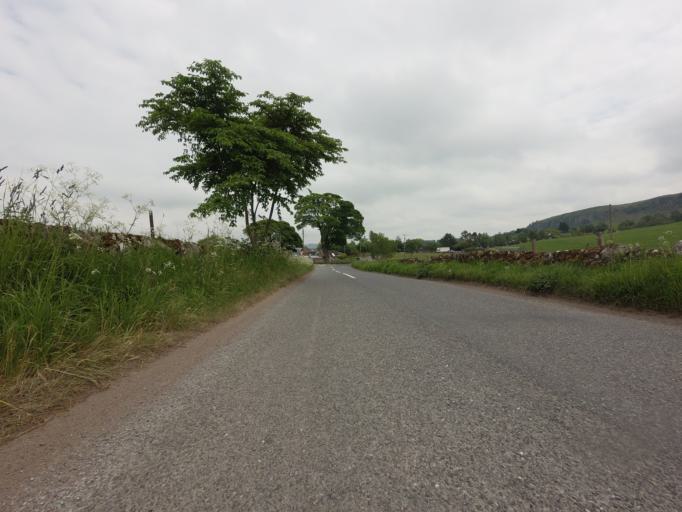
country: GB
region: Scotland
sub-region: Perth and Kinross
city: Kinross
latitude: 56.1645
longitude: -3.4479
